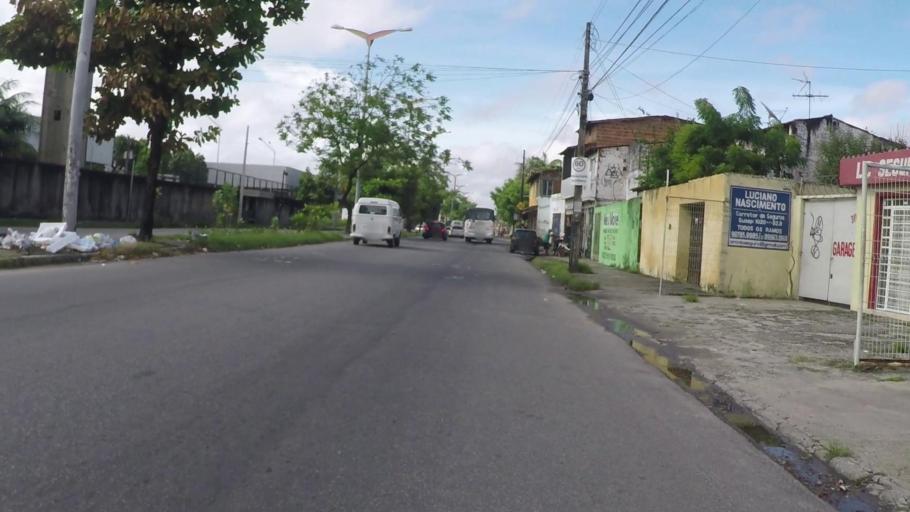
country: BR
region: Ceara
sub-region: Fortaleza
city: Fortaleza
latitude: -3.7306
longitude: -38.5848
